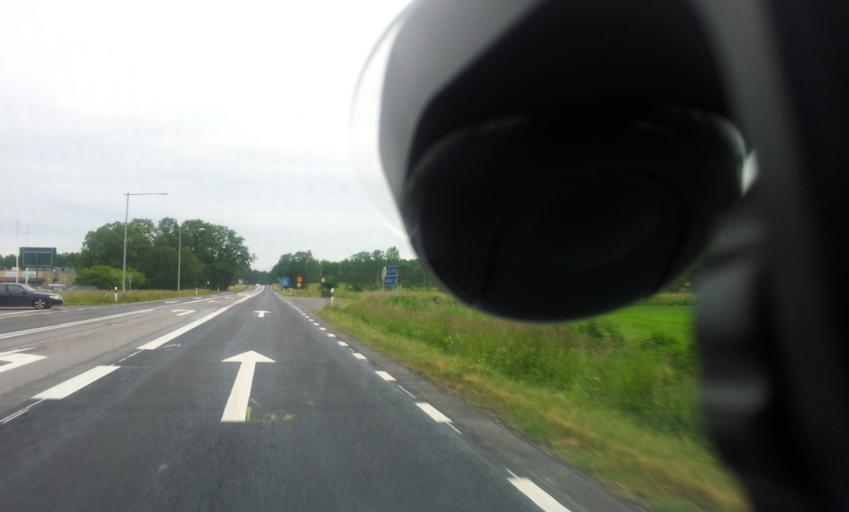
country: SE
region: Kalmar
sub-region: Monsteras Kommun
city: Moensteras
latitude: 57.0289
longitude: 16.4318
